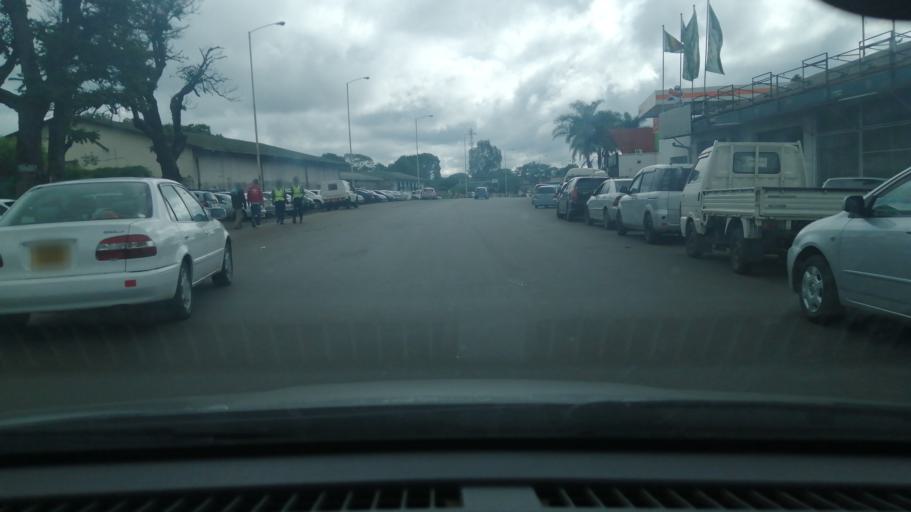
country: ZW
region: Harare
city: Harare
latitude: -17.8303
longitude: 31.0580
